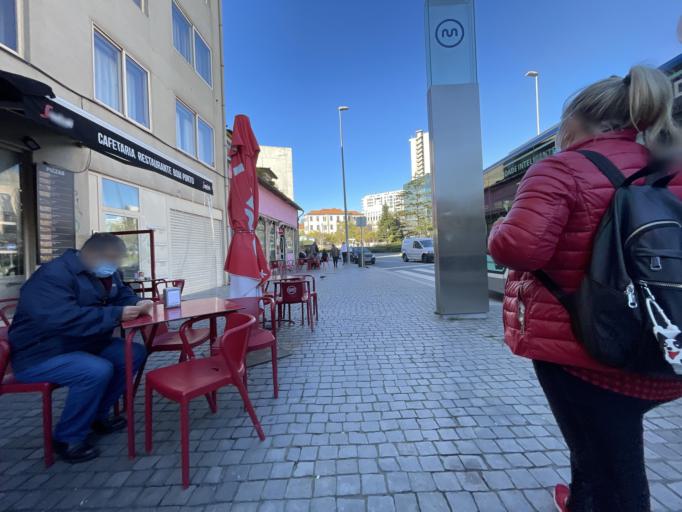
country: PT
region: Porto
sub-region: Porto
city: Porto
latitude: 41.1488
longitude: -8.5989
